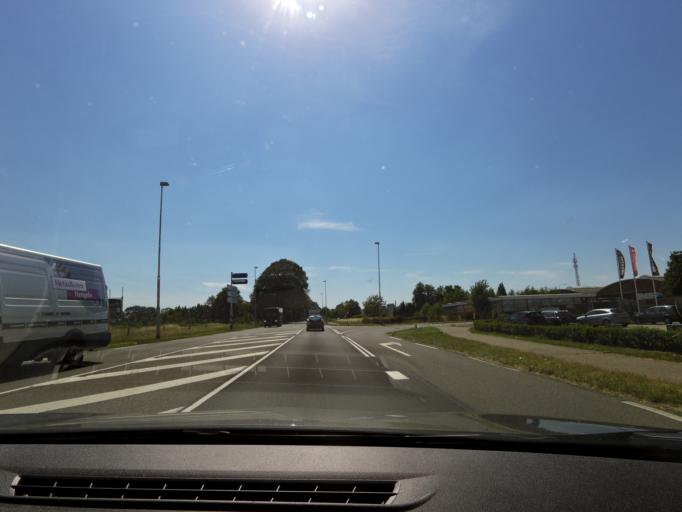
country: NL
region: Gelderland
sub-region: Berkelland
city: Eibergen
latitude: 52.0902
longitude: 6.6468
